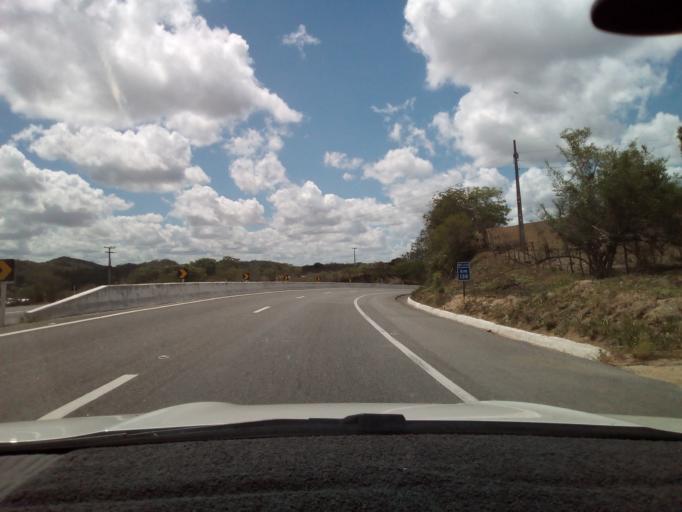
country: BR
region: Paraiba
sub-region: Massaranduba
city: Massaranduba
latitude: -7.2700
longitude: -35.7890
